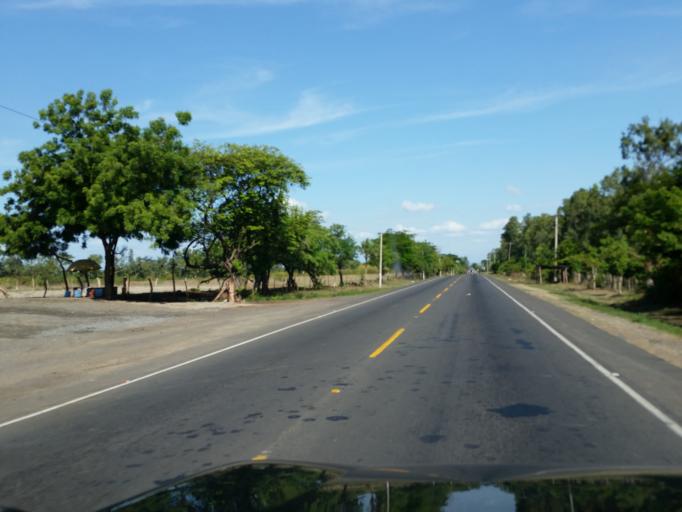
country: NI
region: Leon
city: La Paz Centro
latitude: 12.3295
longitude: -86.8045
